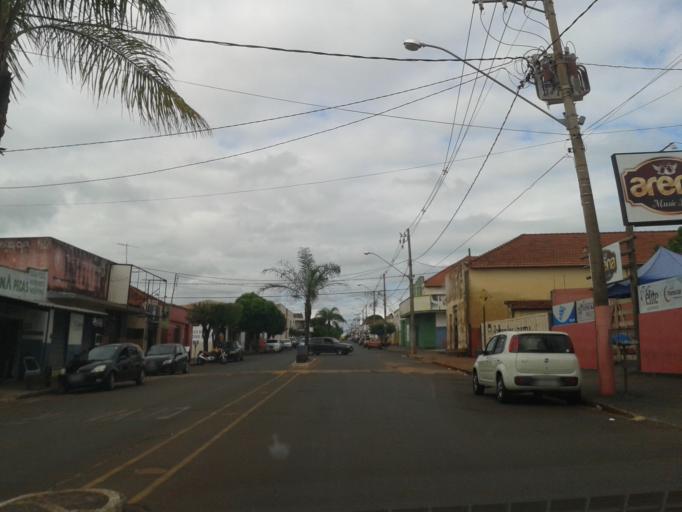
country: BR
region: Minas Gerais
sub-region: Ituiutaba
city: Ituiutaba
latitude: -18.9782
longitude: -49.4767
